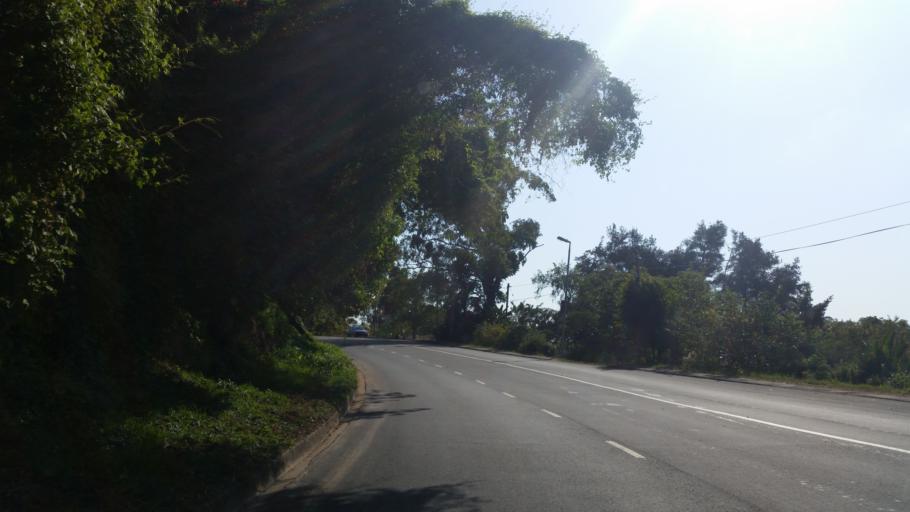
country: ZA
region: KwaZulu-Natal
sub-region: eThekwini Metropolitan Municipality
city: Berea
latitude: -29.8264
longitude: 30.9131
